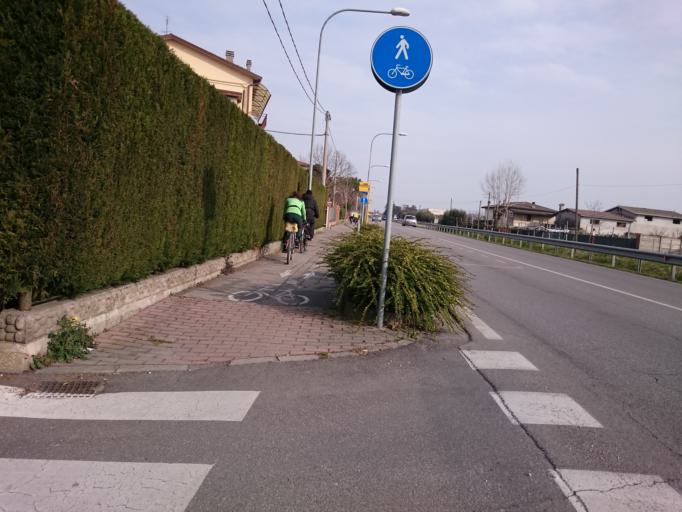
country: IT
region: Veneto
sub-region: Provincia di Padova
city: Caselle
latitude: 45.4104
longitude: 11.8179
